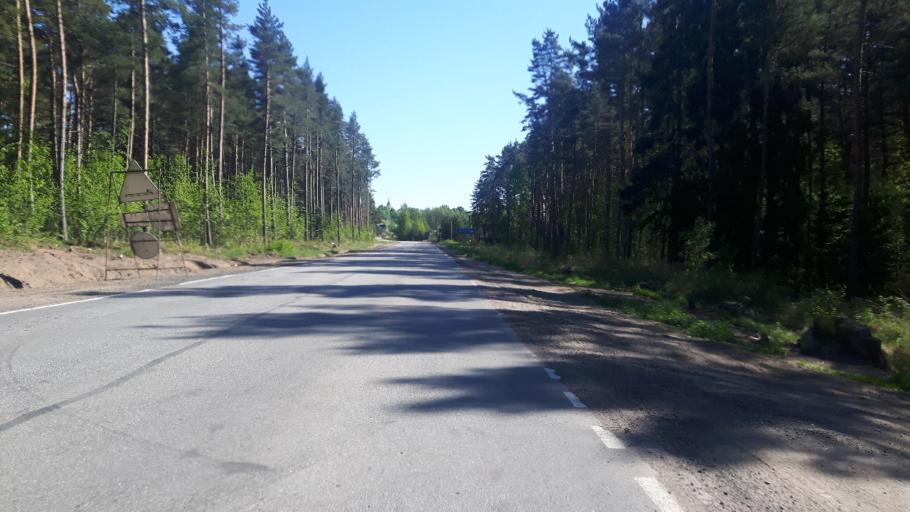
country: RU
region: Leningrad
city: Sosnovyy Bor
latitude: 60.2248
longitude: 29.0066
